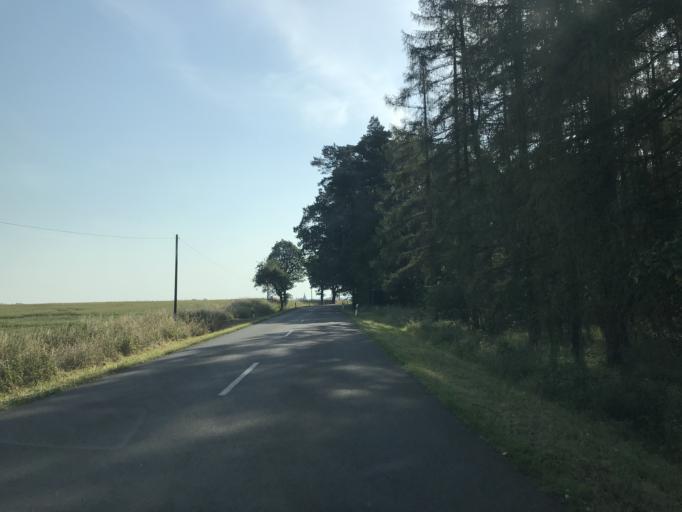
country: DE
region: Saxony-Anhalt
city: Erxleben
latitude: 52.2484
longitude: 11.2019
